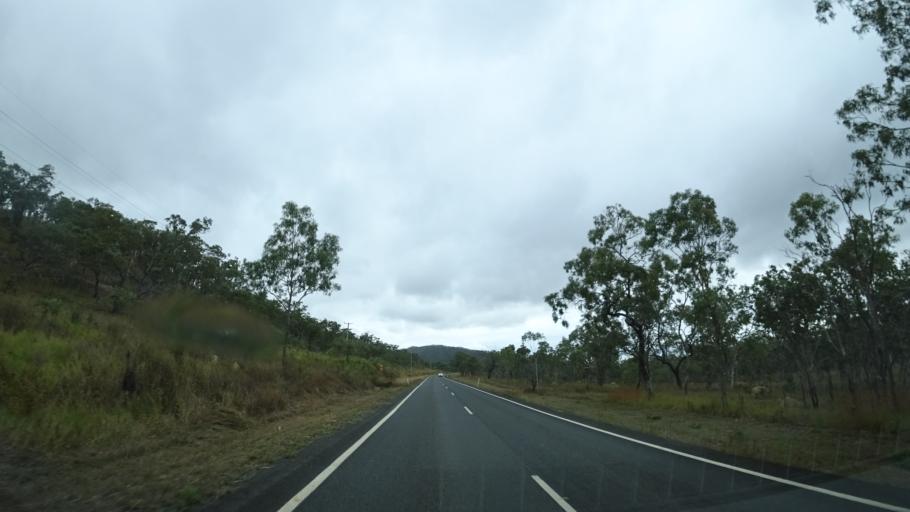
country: AU
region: Queensland
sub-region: Cairns
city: Port Douglas
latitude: -16.7128
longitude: 145.3512
